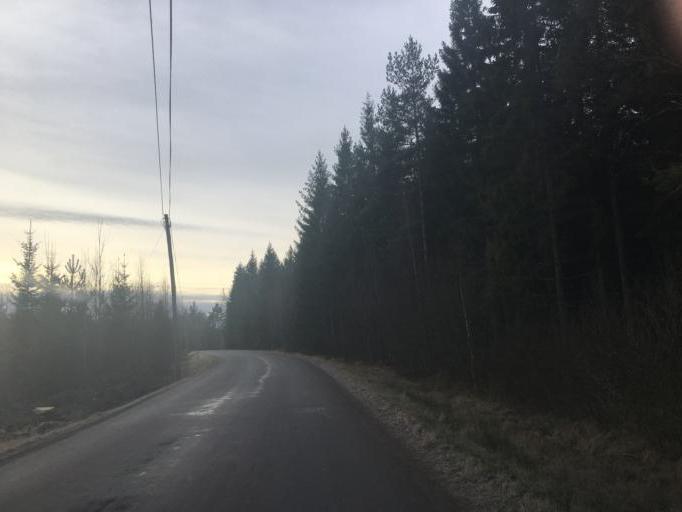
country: SE
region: OEstergoetland
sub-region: Norrkopings Kommun
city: Kimstad
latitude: 58.4305
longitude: 16.0704
